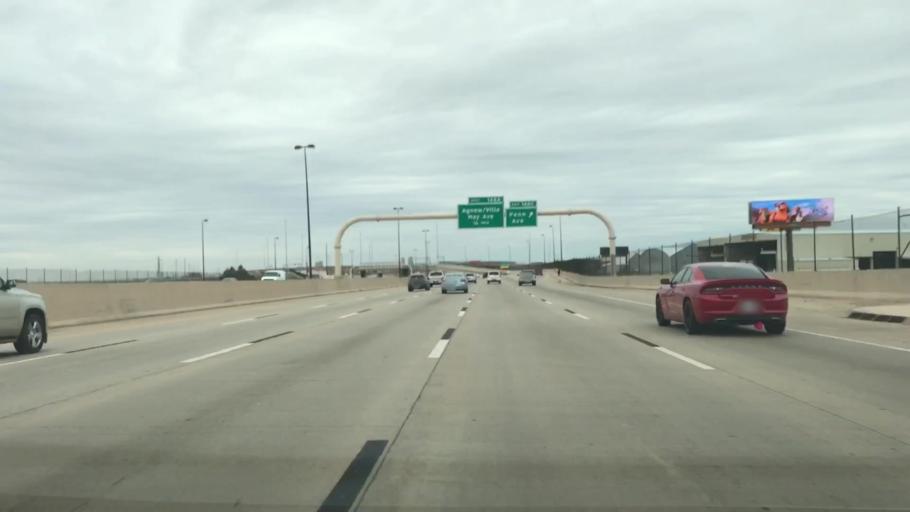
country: US
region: Oklahoma
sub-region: Oklahoma County
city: Oklahoma City
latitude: 35.4610
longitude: -97.5411
